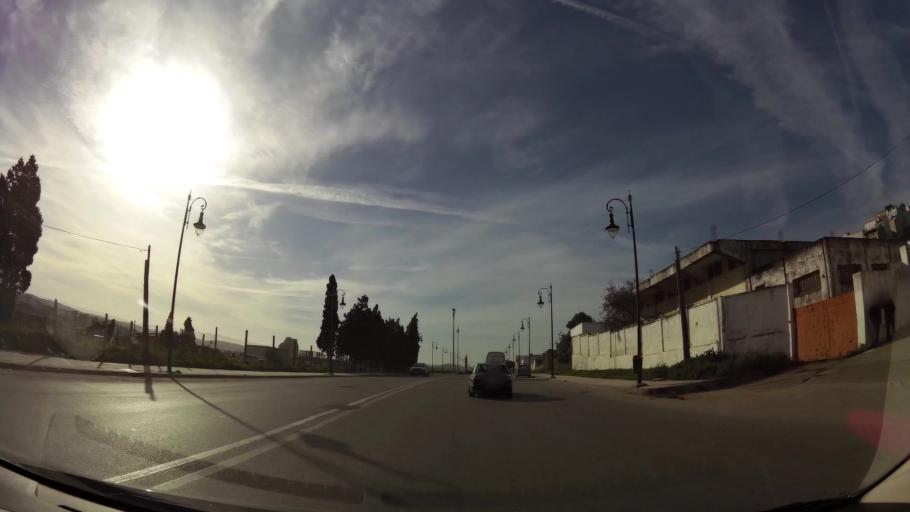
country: MA
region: Tanger-Tetouan
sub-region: Tanger-Assilah
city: Tangier
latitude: 35.7680
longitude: -5.7860
